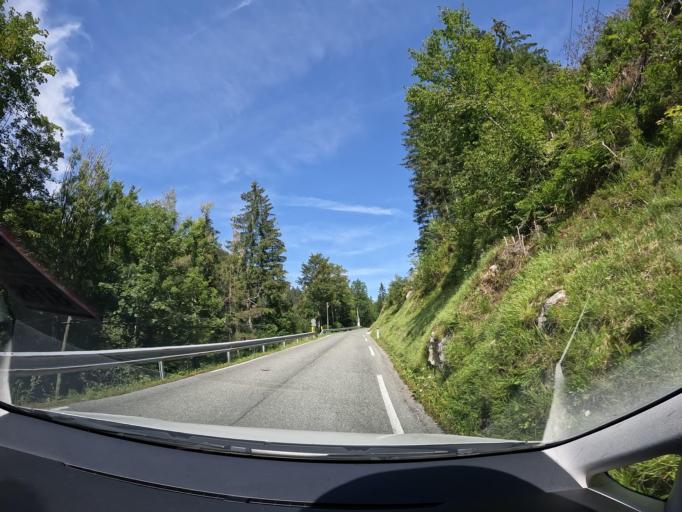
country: AT
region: Carinthia
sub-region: Politischer Bezirk Villach Land
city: Sankt Jakob
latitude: 46.5588
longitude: 14.0775
